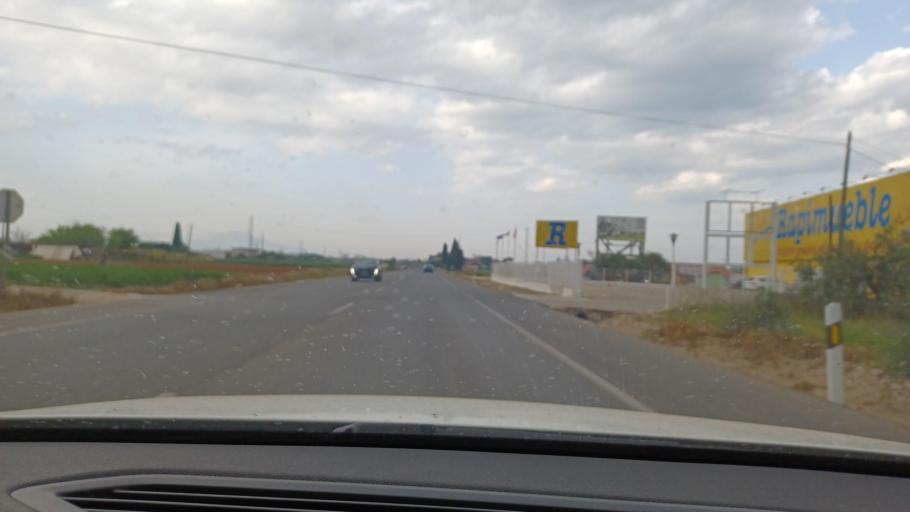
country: ES
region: Valencia
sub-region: Provincia de Castello
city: Benicarlo
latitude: 40.4429
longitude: 0.4450
